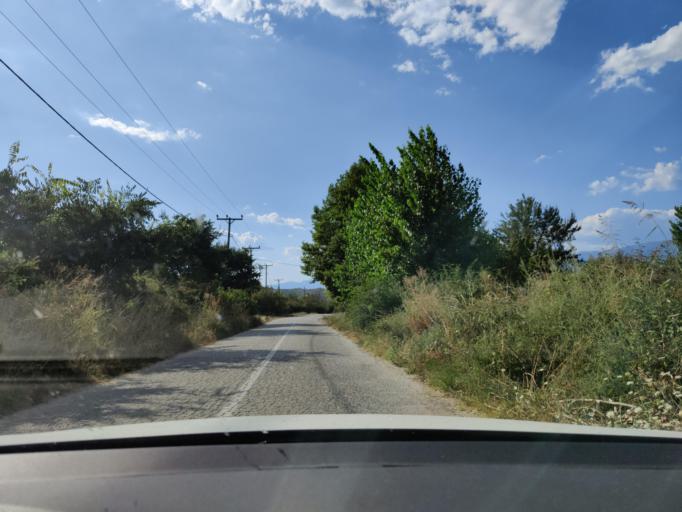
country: GR
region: Central Macedonia
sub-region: Nomos Serron
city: Chrysochorafa
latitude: 41.1816
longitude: 23.1069
